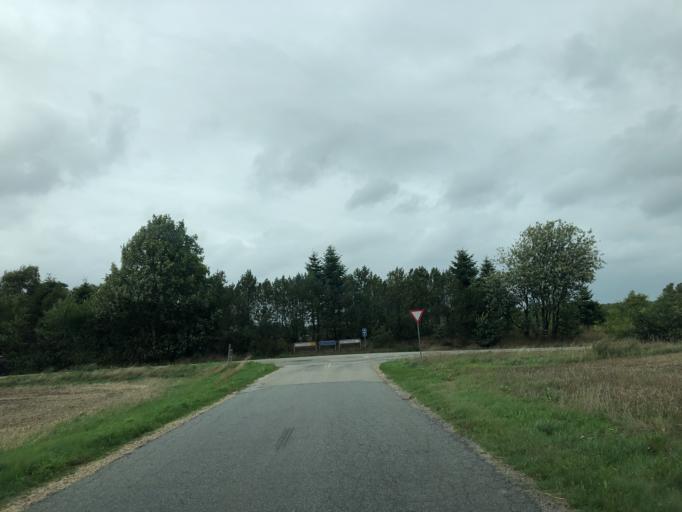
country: DK
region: Central Jutland
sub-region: Herning Kommune
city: Lind
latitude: 56.0895
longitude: 8.9539
